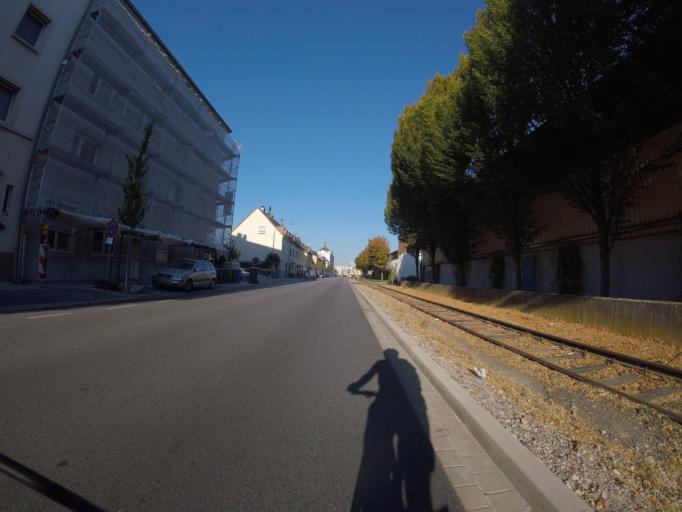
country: DE
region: Rheinland-Pfalz
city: Ludwigshafen am Rhein
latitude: 49.4689
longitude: 8.4511
